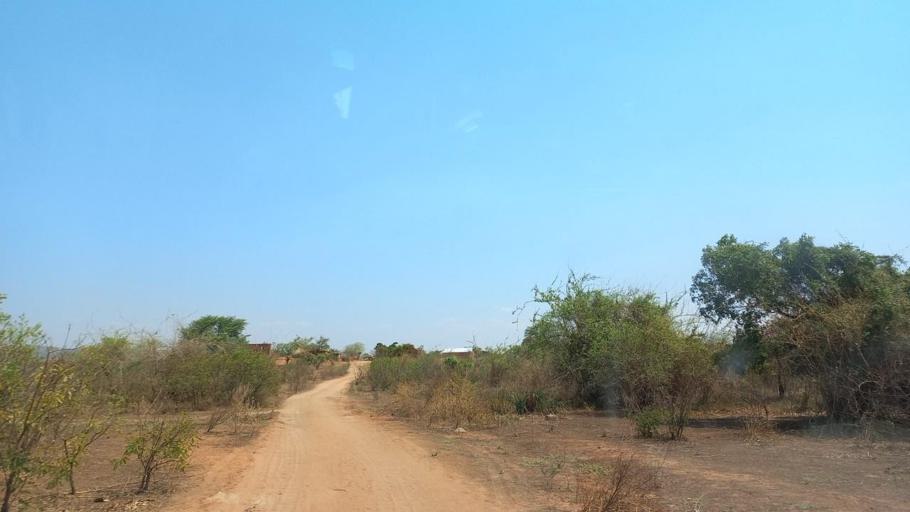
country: ZM
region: Lusaka
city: Luangwa
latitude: -15.6009
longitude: 30.4018
